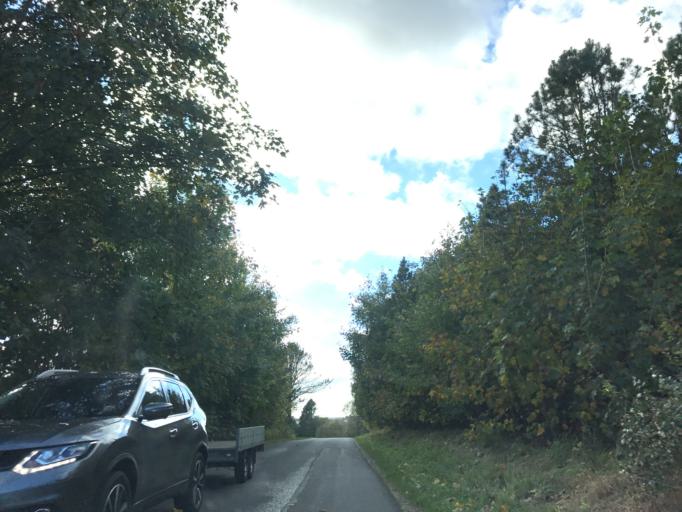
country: DK
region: Central Jutland
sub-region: Silkeborg Kommune
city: Kjellerup
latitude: 56.2580
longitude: 9.4823
